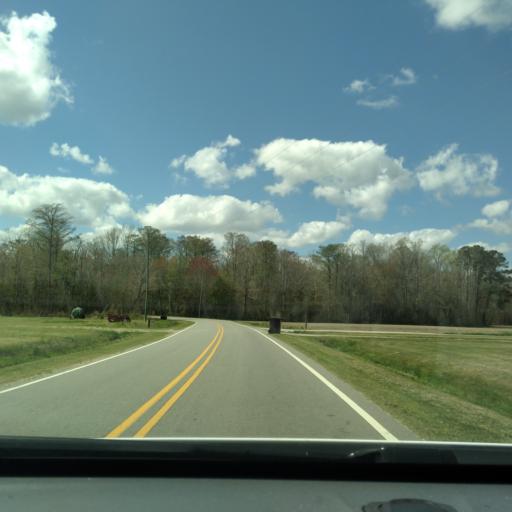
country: US
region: North Carolina
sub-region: Washington County
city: Plymouth
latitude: 35.8429
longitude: -76.7281
